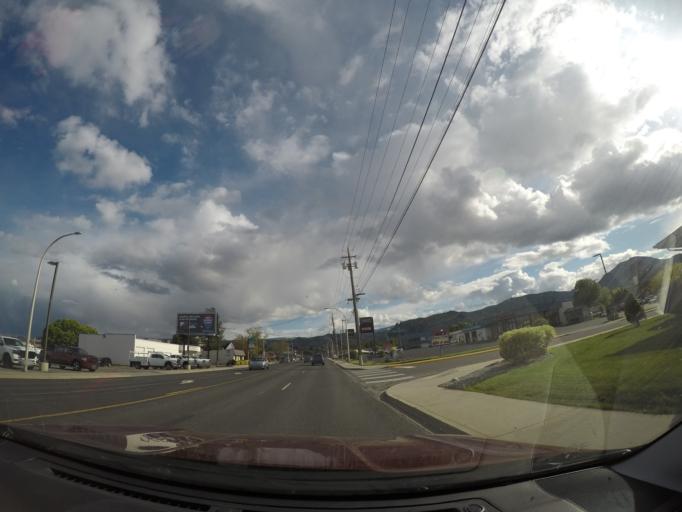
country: US
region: Washington
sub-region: Chelan County
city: Wenatchee
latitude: 47.4352
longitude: -120.3250
